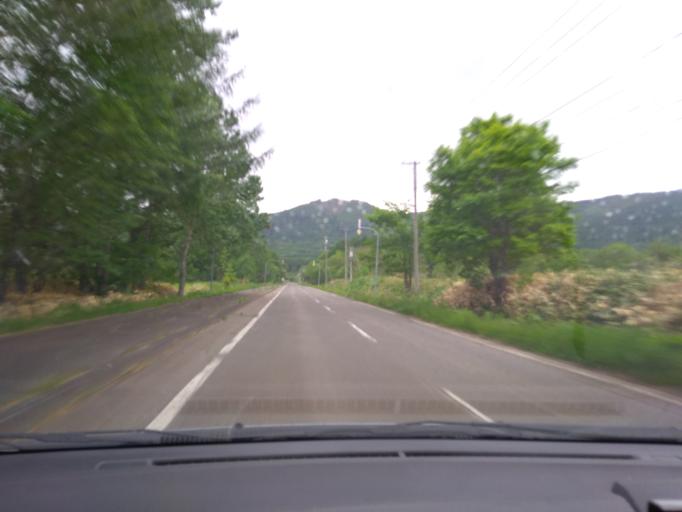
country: JP
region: Hokkaido
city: Shimo-furano
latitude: 43.1762
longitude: 142.5296
